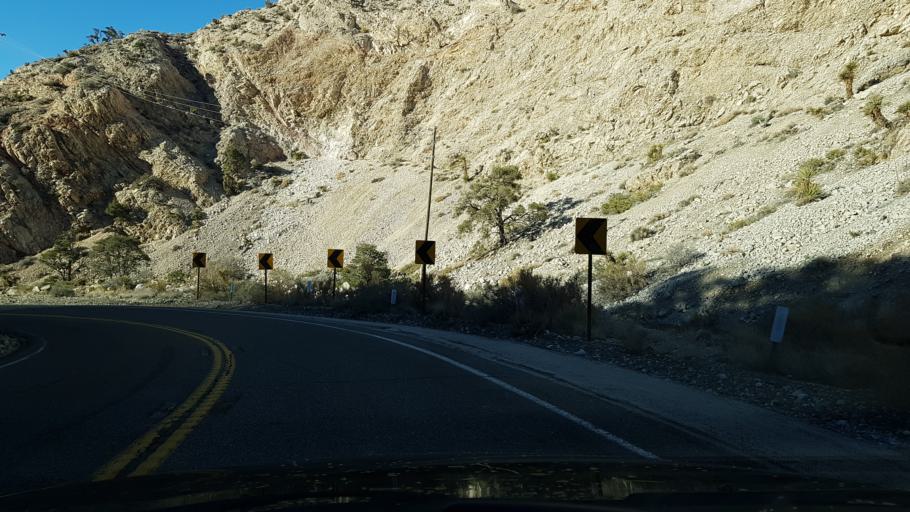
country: US
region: California
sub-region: San Bernardino County
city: Big Bear City
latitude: 34.3473
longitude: -116.8437
